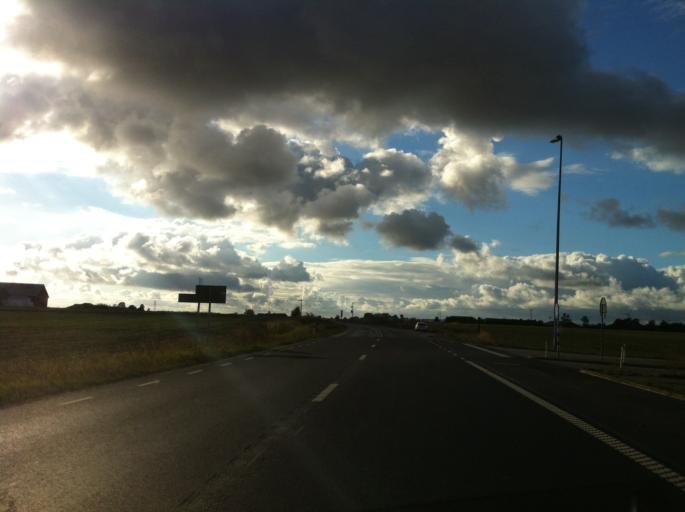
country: SE
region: Skane
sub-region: Svalovs Kommun
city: Teckomatorp
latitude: 55.8760
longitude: 13.0742
